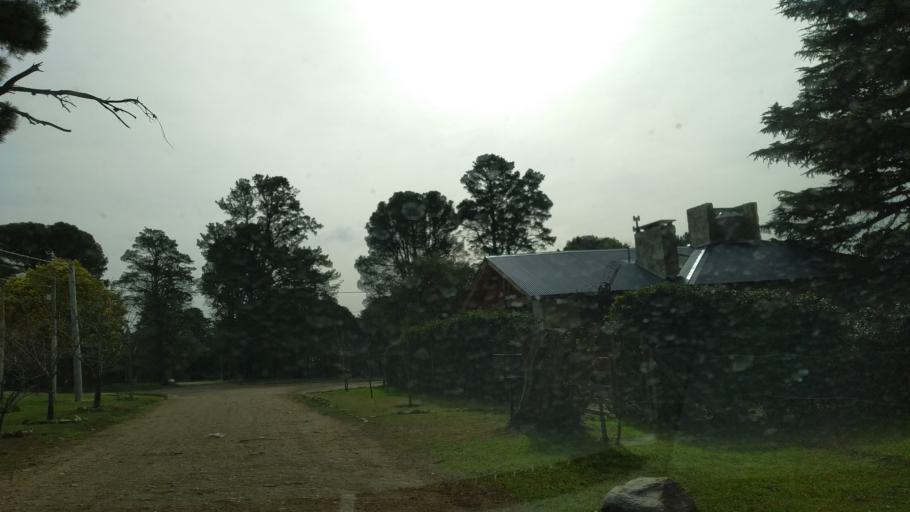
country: AR
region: Buenos Aires
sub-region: Partido de Tornquist
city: Tornquist
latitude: -38.0855
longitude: -61.9351
